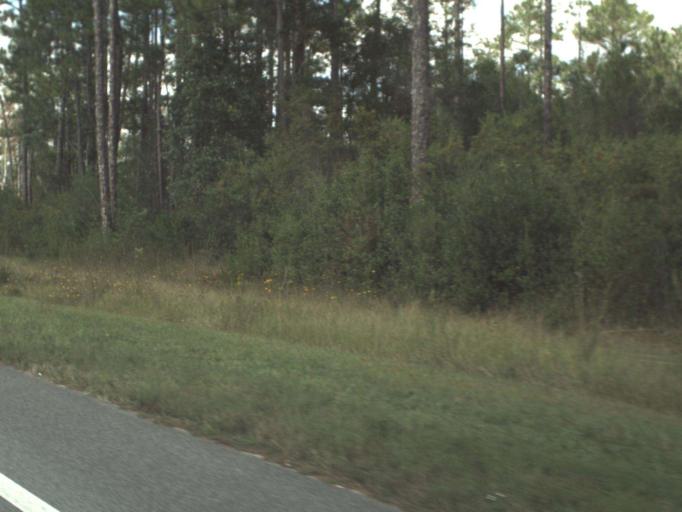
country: US
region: Florida
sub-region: Walton County
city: Freeport
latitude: 30.4756
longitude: -86.0158
